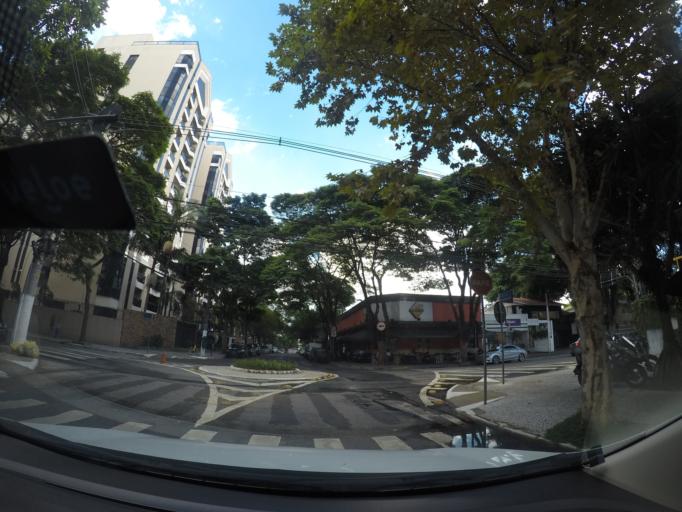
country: BR
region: Sao Paulo
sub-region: Sao Paulo
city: Sao Paulo
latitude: -23.5900
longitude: -46.6704
